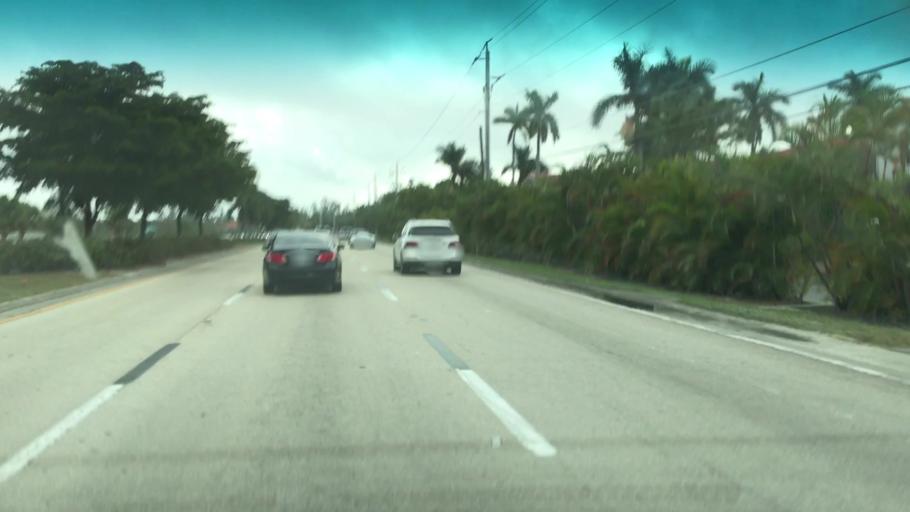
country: US
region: Florida
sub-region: Lee County
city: Cypress Lake
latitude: 26.5206
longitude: -81.8840
